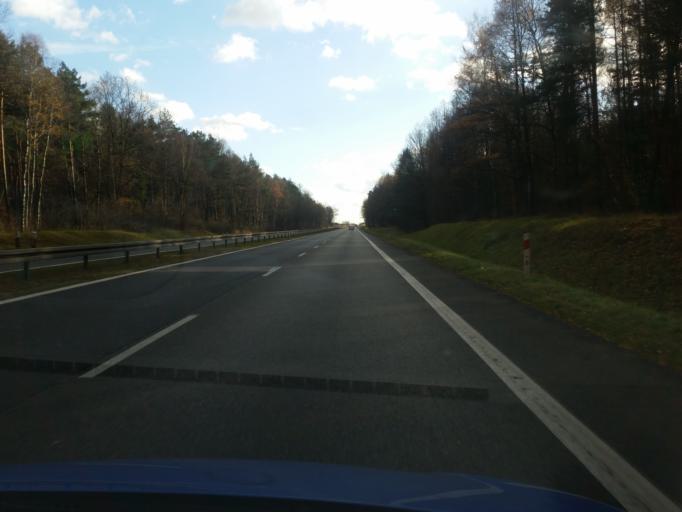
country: PL
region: Silesian Voivodeship
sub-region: Powiat czestochowski
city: Kamienica Polska
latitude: 50.6481
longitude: 19.1336
